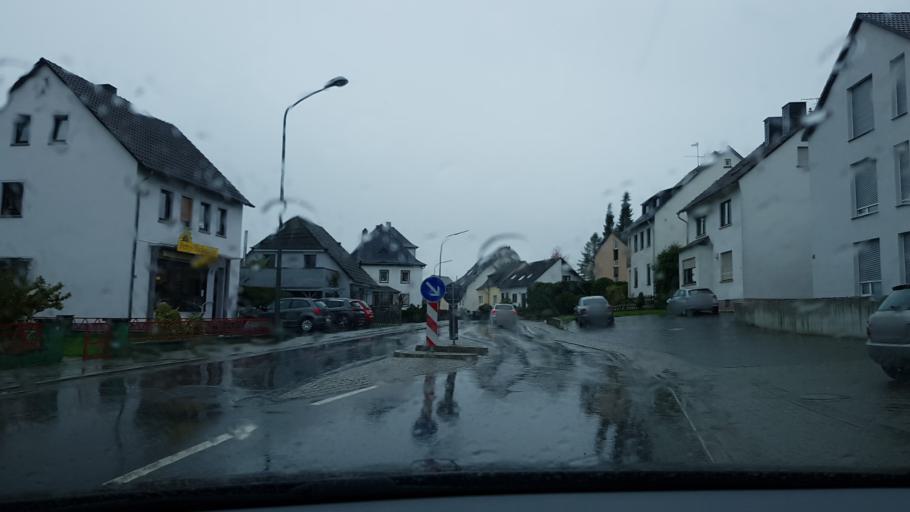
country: DE
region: Rheinland-Pfalz
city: Neuerburg
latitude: 49.9749
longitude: 6.9388
